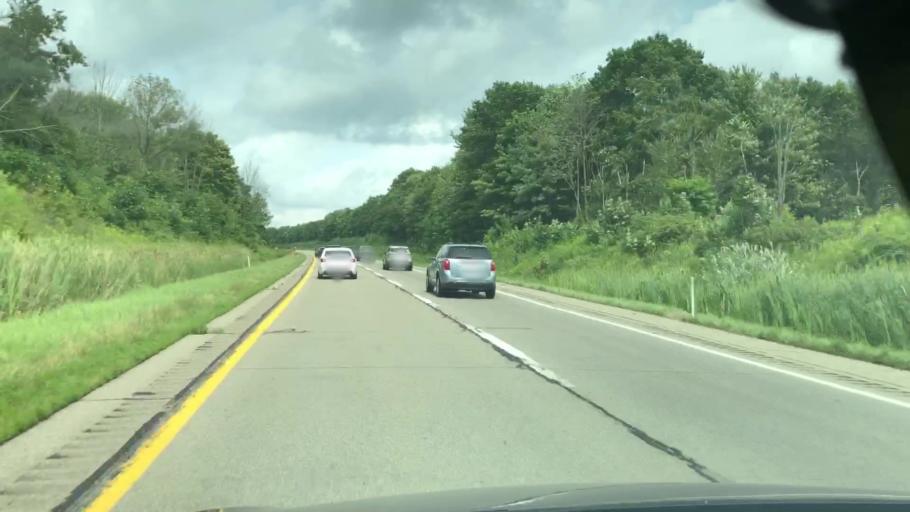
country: US
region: Pennsylvania
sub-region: Erie County
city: Edinboro
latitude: 41.7843
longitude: -80.1793
